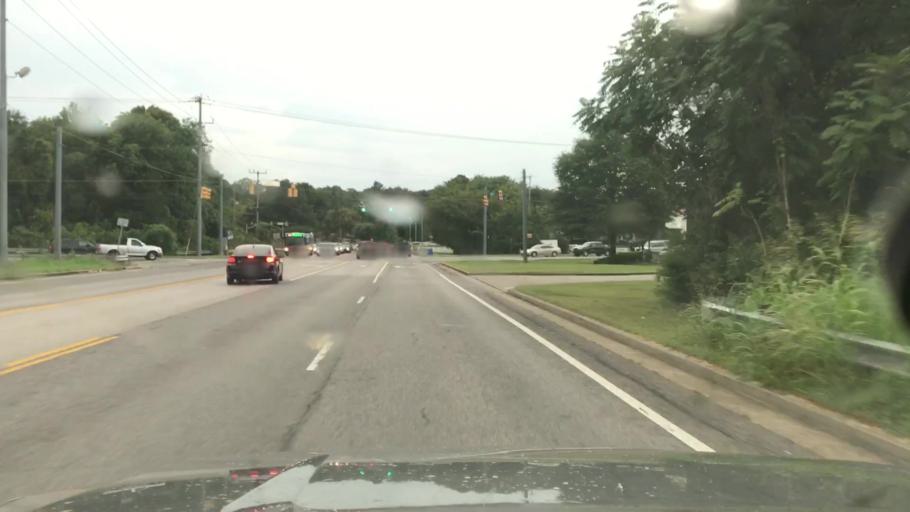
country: US
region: Tennessee
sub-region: Rutherford County
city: La Vergne
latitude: 36.0909
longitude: -86.6260
